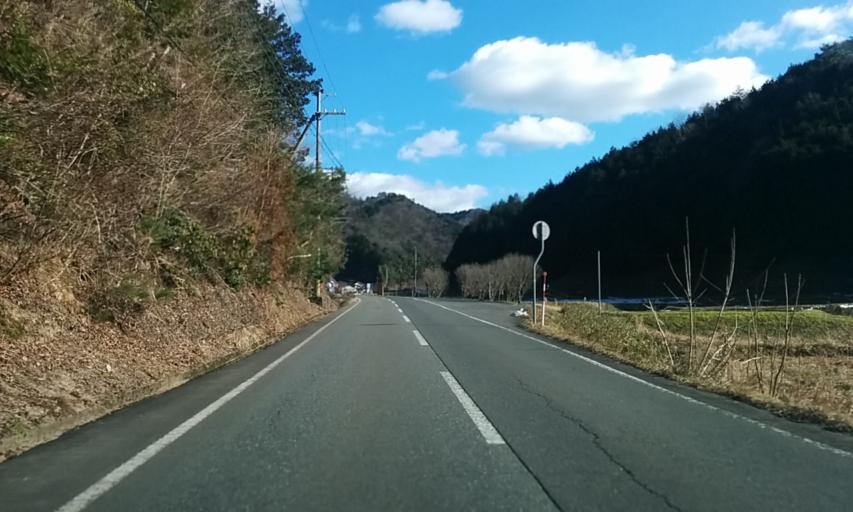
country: JP
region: Hyogo
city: Toyooka
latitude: 35.4319
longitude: 134.9530
